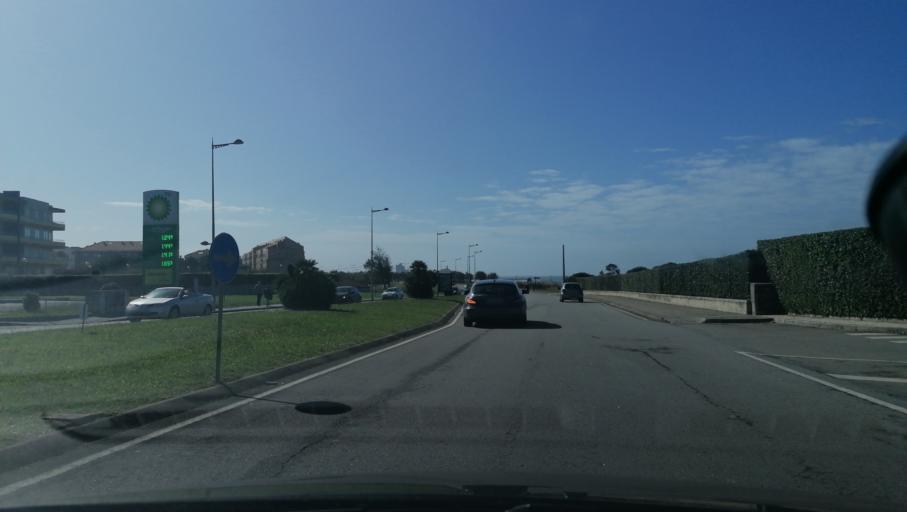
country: PT
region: Aveiro
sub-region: Espinho
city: Espinho
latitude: 41.0278
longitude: -8.6424
